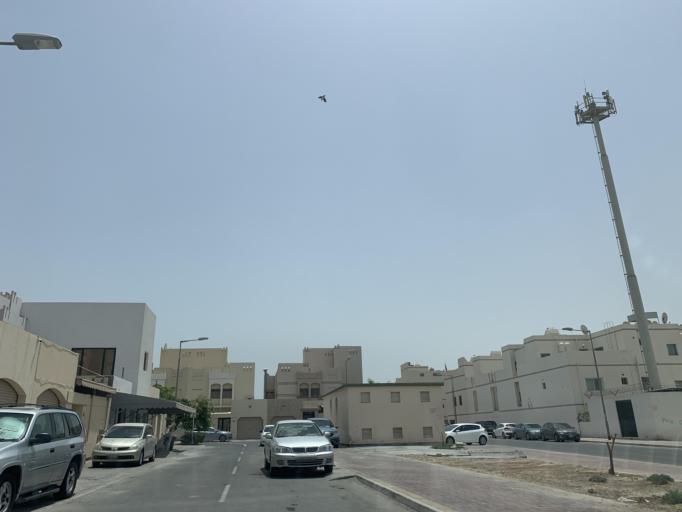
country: BH
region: Northern
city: Sitrah
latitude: 26.1480
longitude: 50.5880
